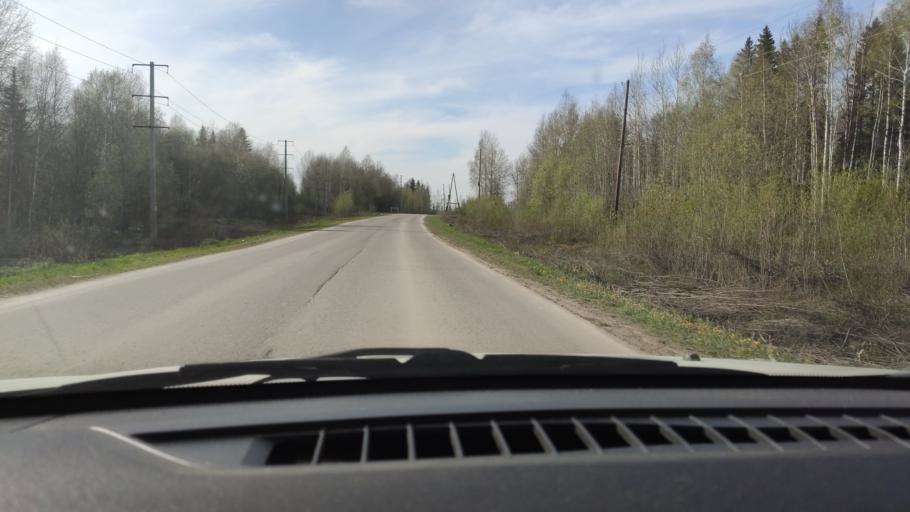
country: RU
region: Perm
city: Novyye Lyady
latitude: 57.9294
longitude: 56.6484
